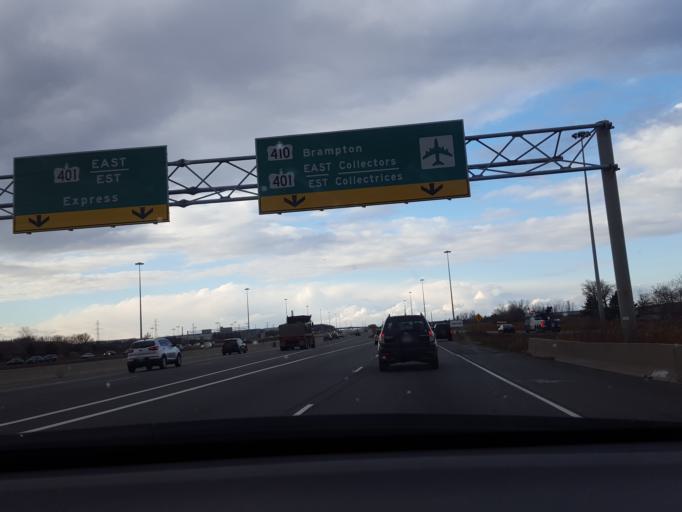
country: CA
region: Ontario
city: Mississauga
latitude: 43.6234
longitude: -79.6382
